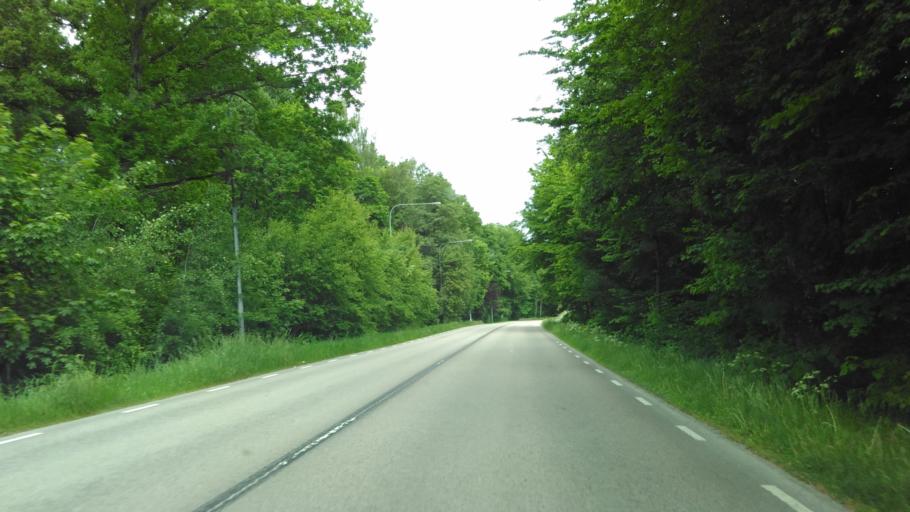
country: SE
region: Vaestra Goetaland
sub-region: Lidkopings Kommun
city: Lidkoping
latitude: 58.4851
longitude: 13.1380
